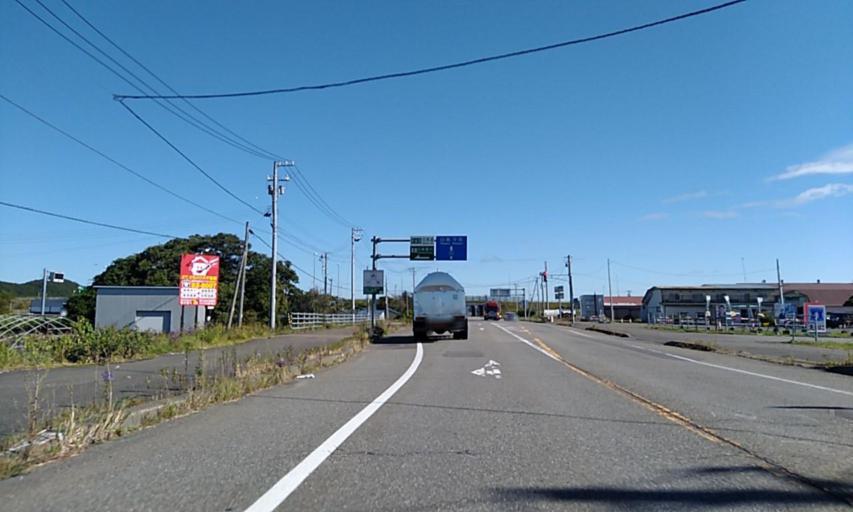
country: JP
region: Hokkaido
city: Shizunai-furukawacho
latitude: 42.5244
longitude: 142.0397
